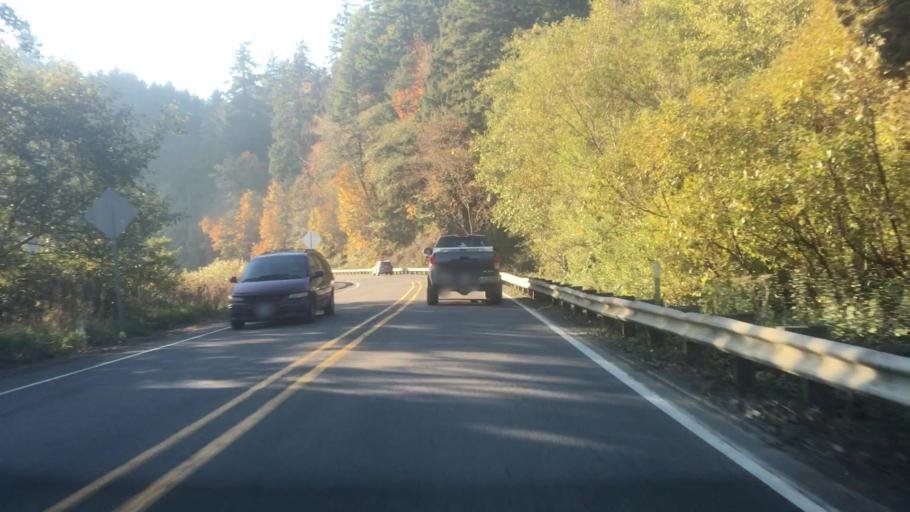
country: US
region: Oregon
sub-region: Clatsop County
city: Astoria
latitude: 46.2492
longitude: -123.8632
